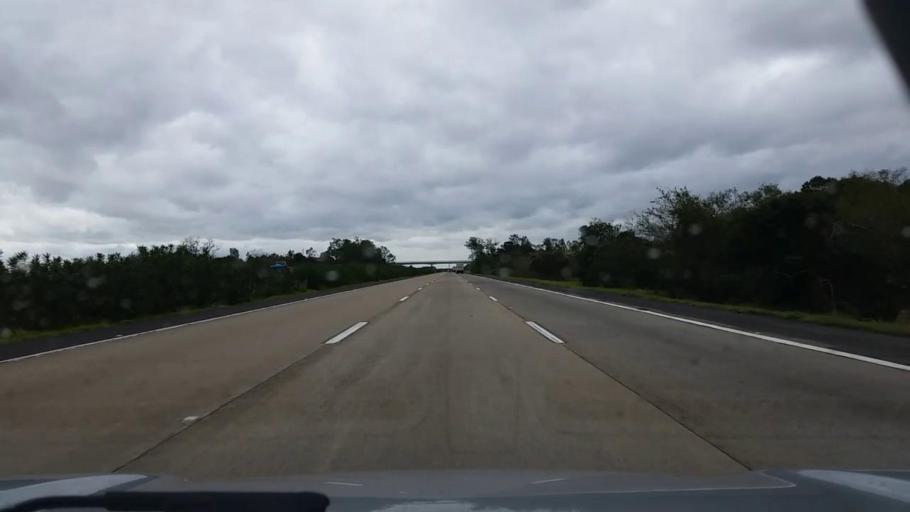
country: BR
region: Rio Grande do Sul
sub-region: Rolante
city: Rolante
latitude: -29.8863
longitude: -50.6497
